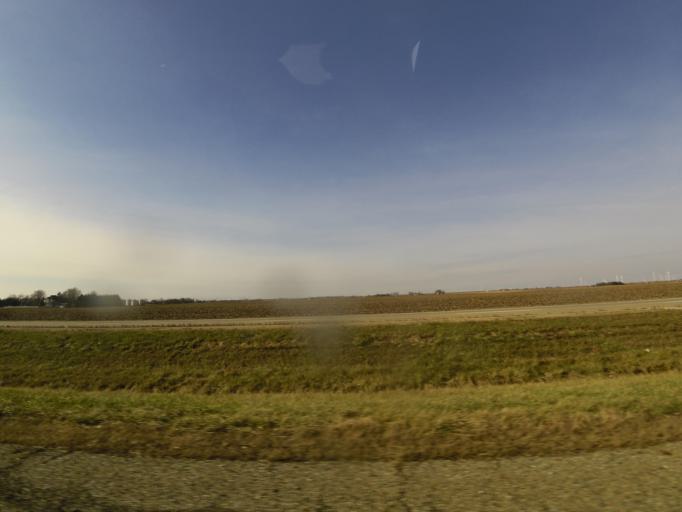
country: US
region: Illinois
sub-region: Macon County
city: Forsyth
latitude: 39.9409
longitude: -88.9555
